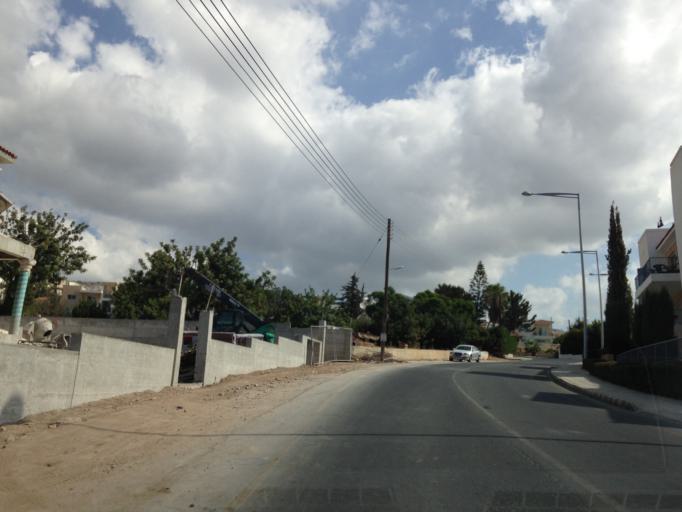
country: CY
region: Pafos
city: Pegeia
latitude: 34.8788
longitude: 32.3752
